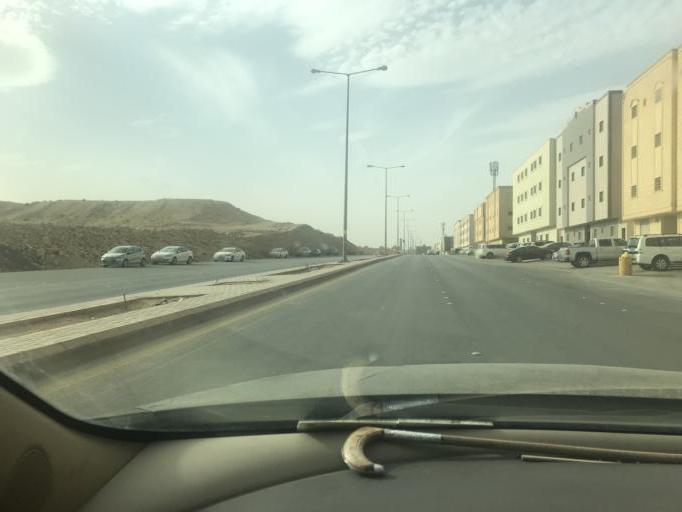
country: SA
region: Ar Riyad
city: Riyadh
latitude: 24.7929
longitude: 46.6691
